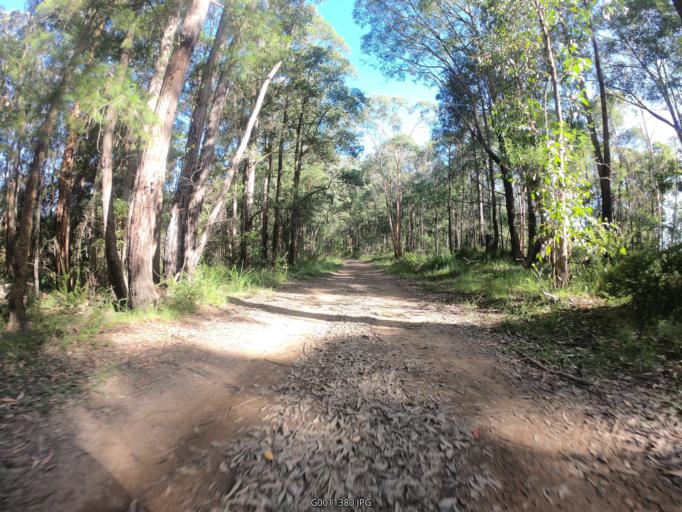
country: AU
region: New South Wales
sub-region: Lake Macquarie Shire
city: Cooranbong
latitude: -33.0258
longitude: 151.3024
